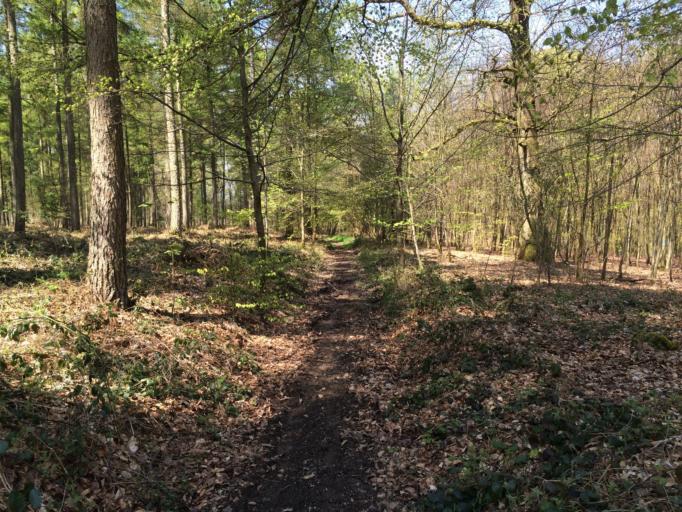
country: BE
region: Wallonia
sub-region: Province de Namur
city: Yvoir
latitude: 50.3394
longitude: 4.9500
